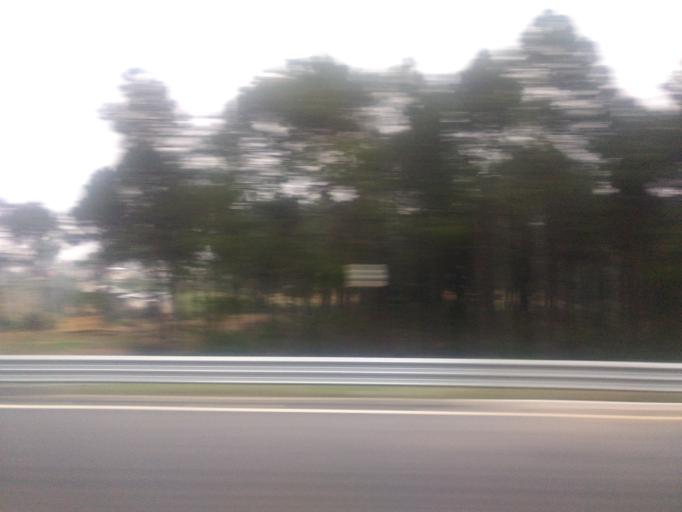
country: MX
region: Veracruz
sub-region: Las Vigas de Ramirez
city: Barrio de San Miguel
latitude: 19.6306
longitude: -97.1166
